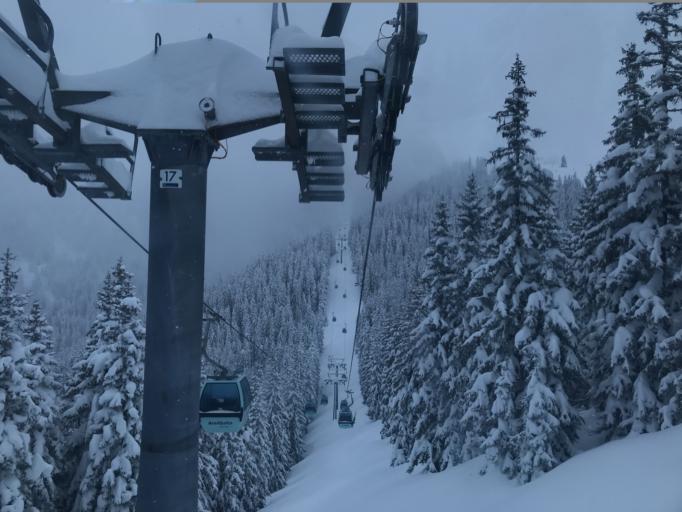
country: AT
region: Salzburg
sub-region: Politischer Bezirk Zell am See
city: Piesendorf
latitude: 47.3172
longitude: 12.7475
